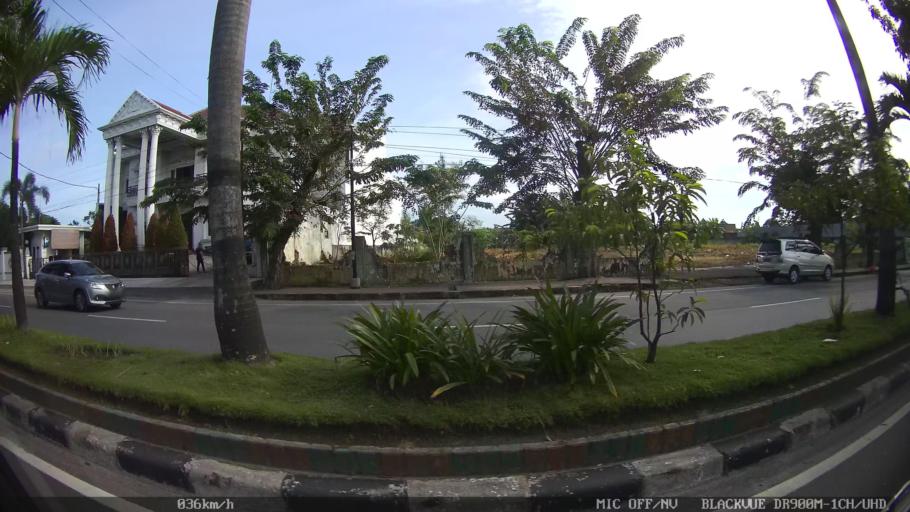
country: ID
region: North Sumatra
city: Medan
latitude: 3.6083
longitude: 98.6499
